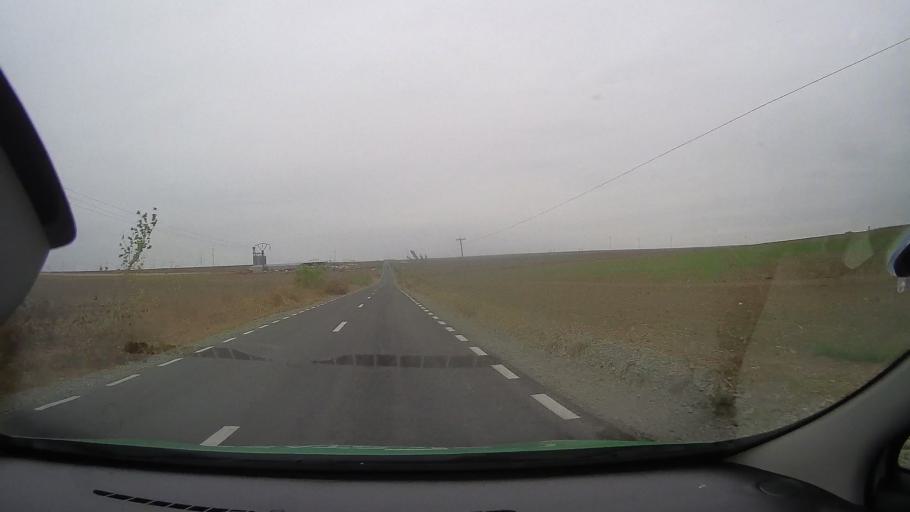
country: RO
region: Constanta
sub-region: Comuna Tortoman
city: Tortoman
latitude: 44.3597
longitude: 28.2106
